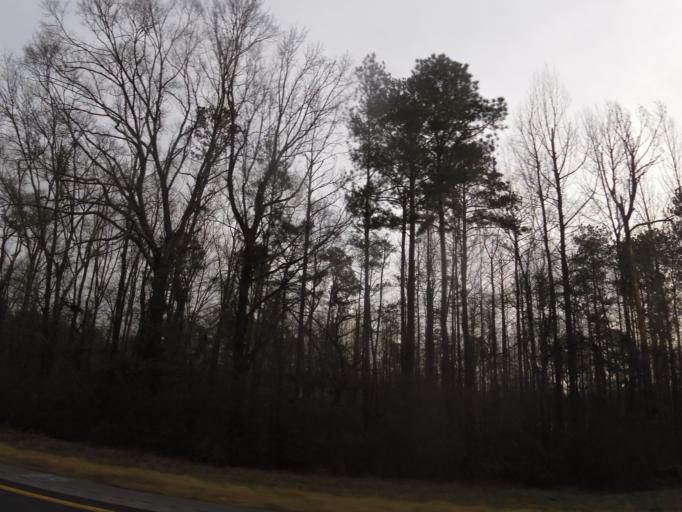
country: US
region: Alabama
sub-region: Chilton County
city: Clanton
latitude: 32.7774
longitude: -86.5705
